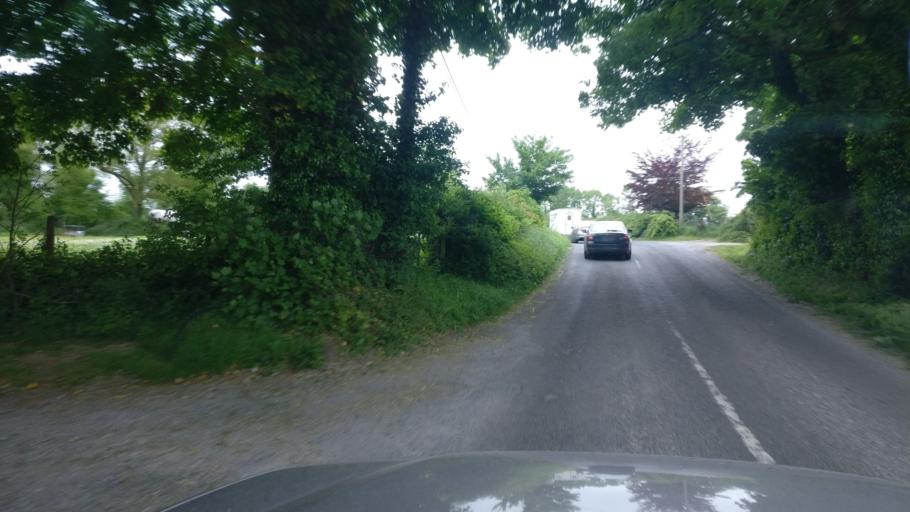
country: IE
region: Connaught
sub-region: County Galway
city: Portumna
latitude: 53.1191
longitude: -8.3138
